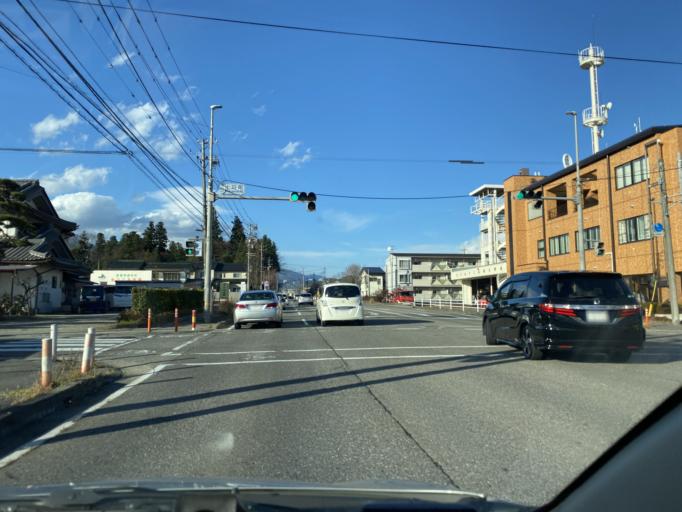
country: JP
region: Nagano
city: Omachi
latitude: 36.5053
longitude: 137.8547
